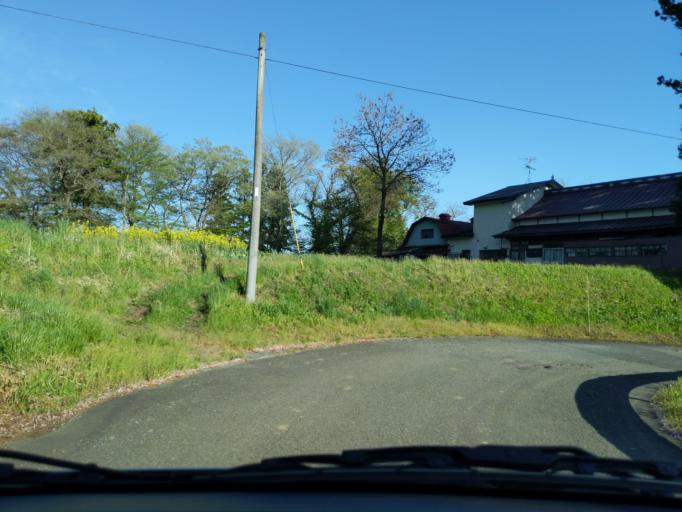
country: JP
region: Iwate
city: Ichinoseki
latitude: 38.8762
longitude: 140.8937
